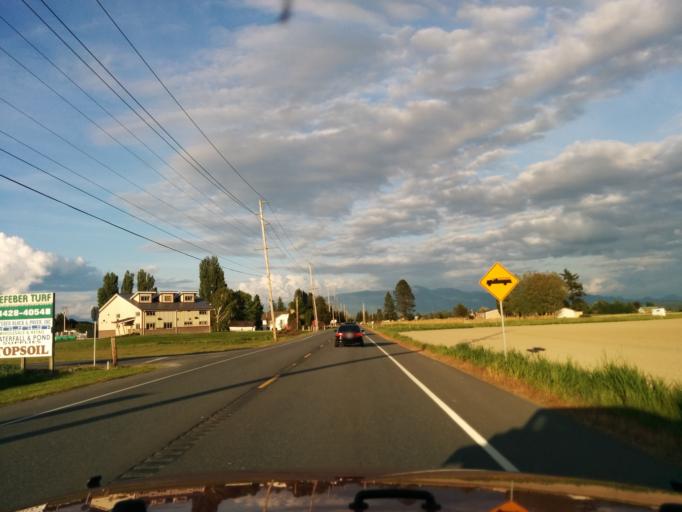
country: US
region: Washington
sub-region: Skagit County
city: Mount Vernon
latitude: 48.4427
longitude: -122.4185
